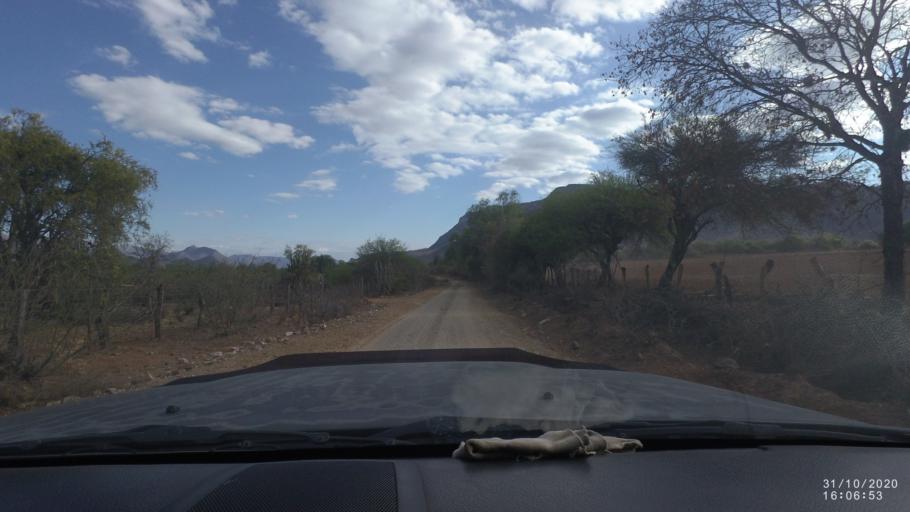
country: BO
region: Chuquisaca
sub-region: Provincia Zudanez
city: Mojocoya
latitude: -18.3762
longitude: -64.6455
